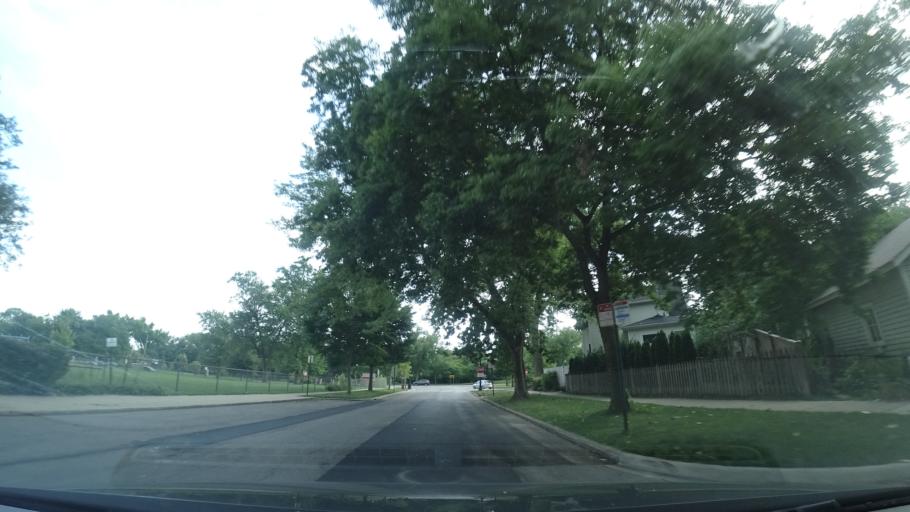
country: US
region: Illinois
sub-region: Cook County
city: Evanston
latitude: 42.0600
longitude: -87.6974
